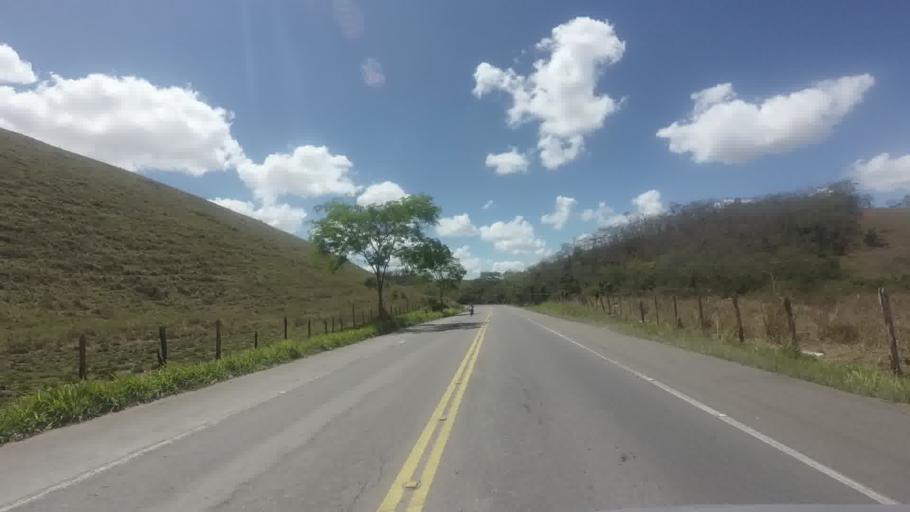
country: BR
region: Rio de Janeiro
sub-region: Santo Antonio De Padua
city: Santo Antonio de Padua
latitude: -21.6586
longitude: -42.3211
